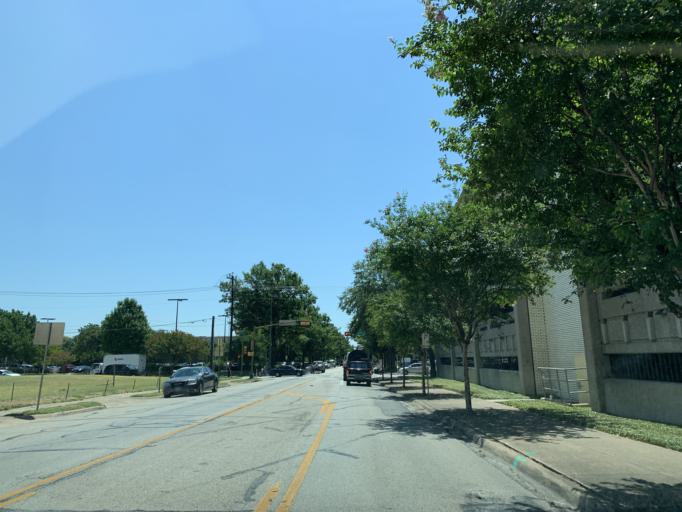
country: US
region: Texas
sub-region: Dallas County
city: Dallas
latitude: 32.7906
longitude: -96.7777
